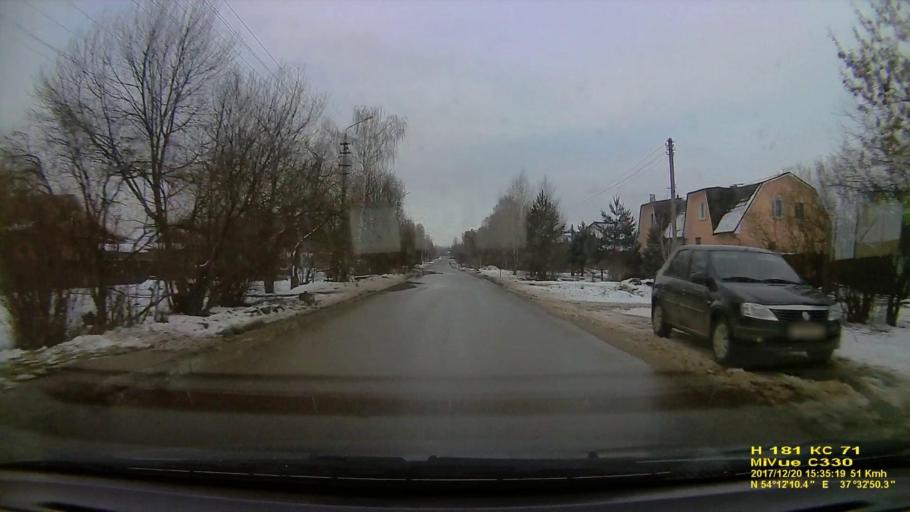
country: RU
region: Tula
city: Tula
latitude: 54.2028
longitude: 37.5475
